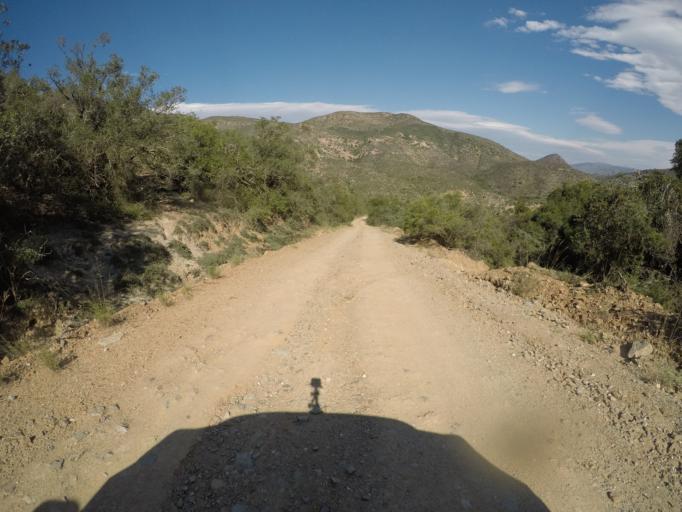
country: ZA
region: Eastern Cape
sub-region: Cacadu District Municipality
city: Kareedouw
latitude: -33.6448
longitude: 24.4571
